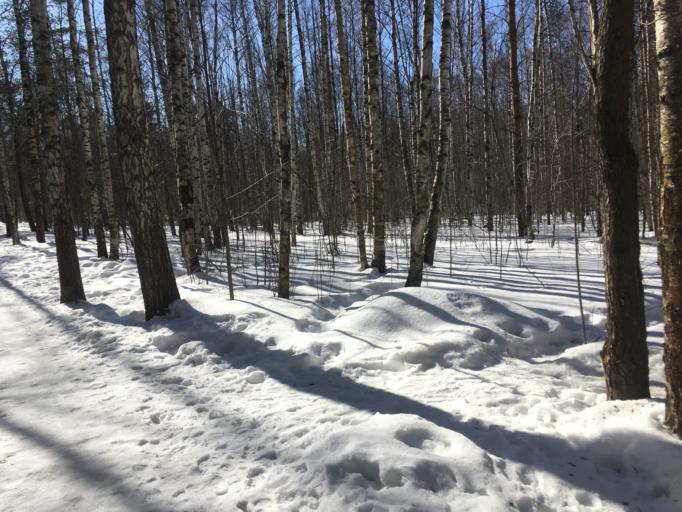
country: RU
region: Perm
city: Kondratovo
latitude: 57.9924
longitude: 56.1638
